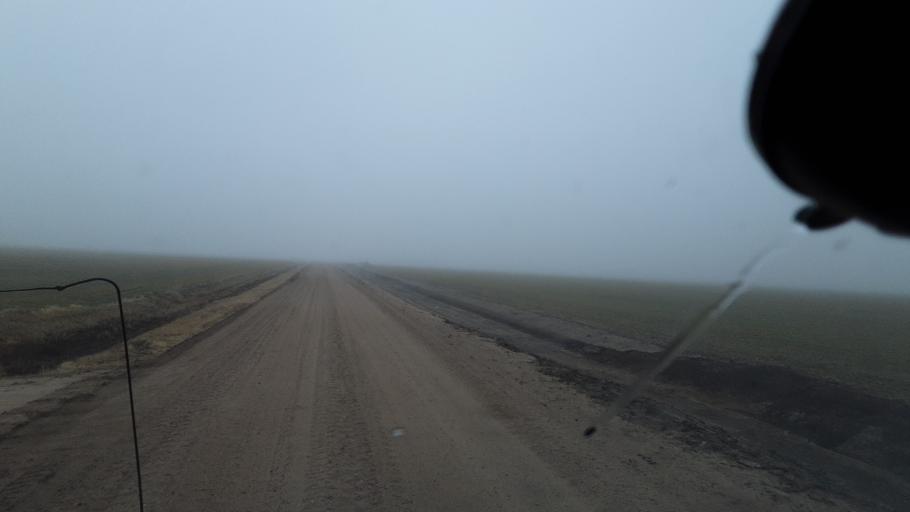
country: US
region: Kansas
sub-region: Reno County
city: South Hutchinson
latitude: 37.9843
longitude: -97.9894
